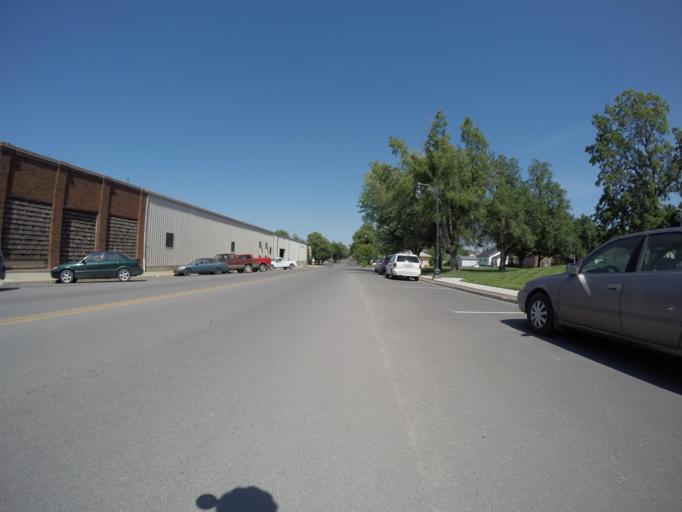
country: US
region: Kansas
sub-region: Nemaha County
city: Sabetha
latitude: 39.9034
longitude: -95.7997
